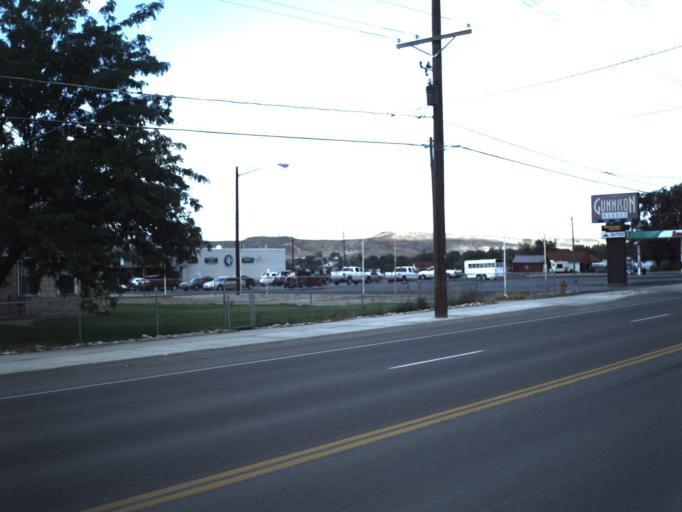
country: US
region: Utah
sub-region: Sanpete County
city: Gunnison
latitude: 39.1444
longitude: -111.8188
